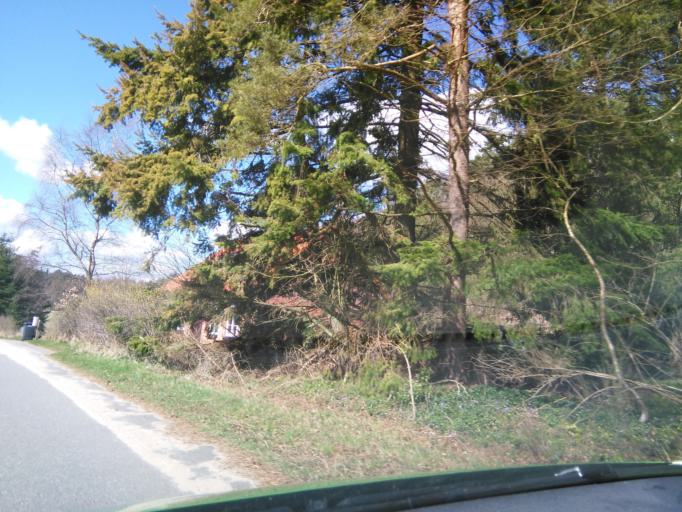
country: DK
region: Central Jutland
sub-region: Silkeborg Kommune
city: Svejbaek
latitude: 56.0733
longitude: 9.6423
